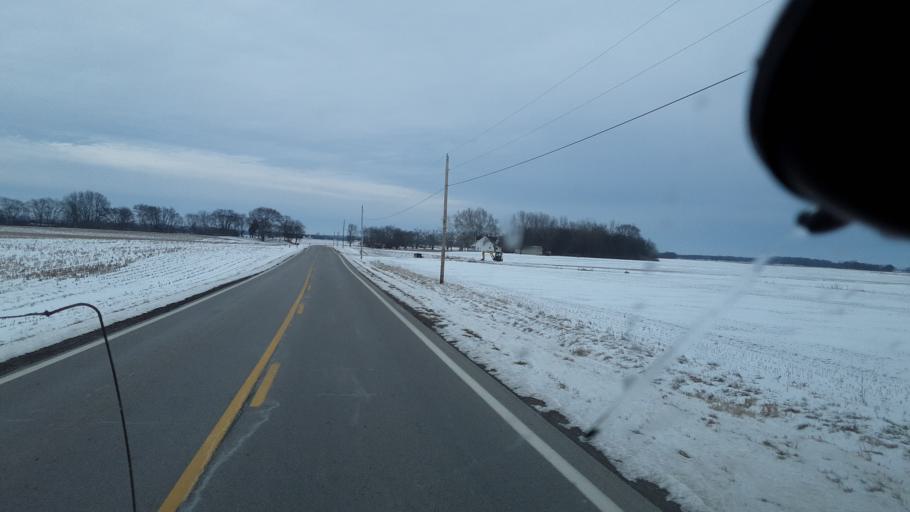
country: US
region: Ohio
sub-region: Pickaway County
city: Circleville
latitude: 39.6230
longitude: -83.0251
